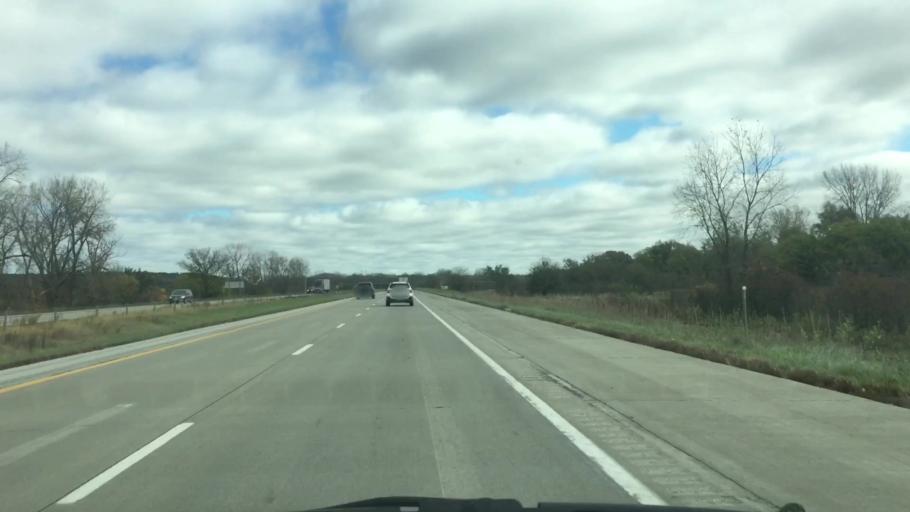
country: US
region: Iowa
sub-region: Polk County
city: Mitchellville
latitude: 41.6817
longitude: -93.3094
